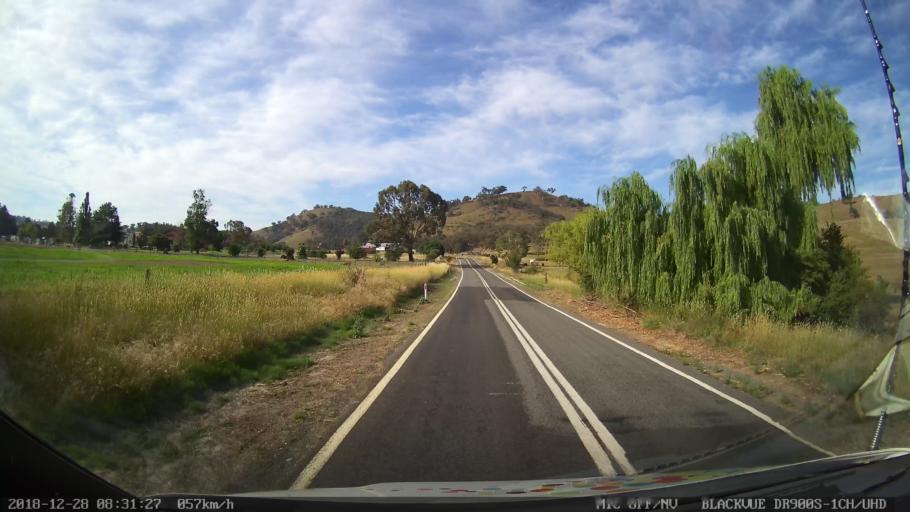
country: AU
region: New South Wales
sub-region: Blayney
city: Blayney
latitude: -33.9592
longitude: 149.3184
